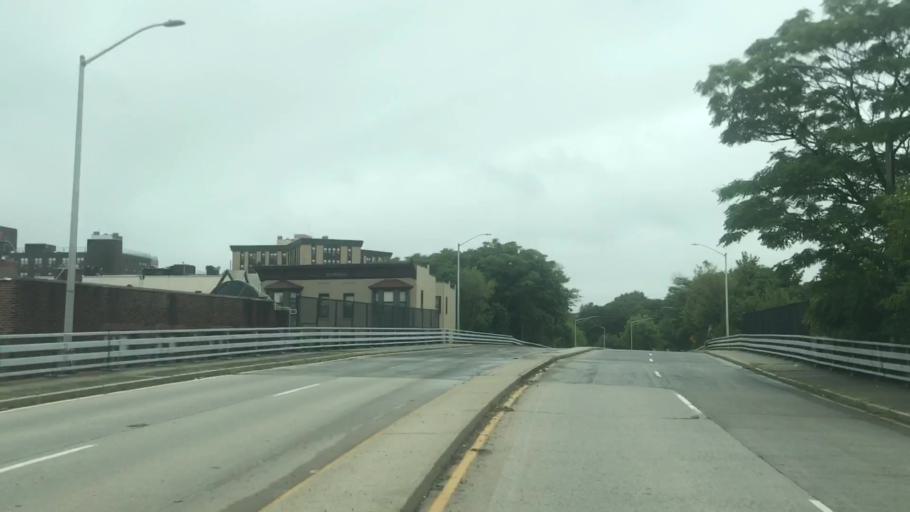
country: US
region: New York
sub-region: Westchester County
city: New Rochelle
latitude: 40.9164
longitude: -73.7833
